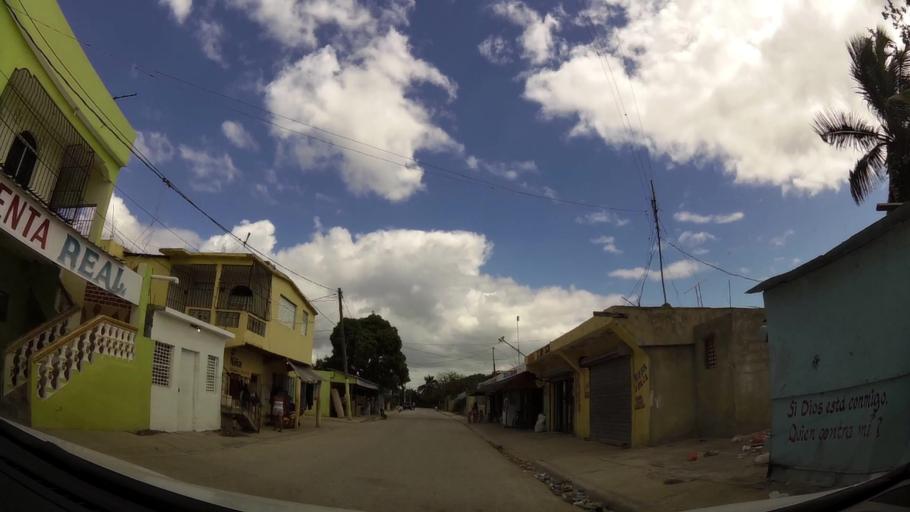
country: DO
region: Santo Domingo
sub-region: Santo Domingo
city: Boca Chica
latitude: 18.4504
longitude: -69.6354
